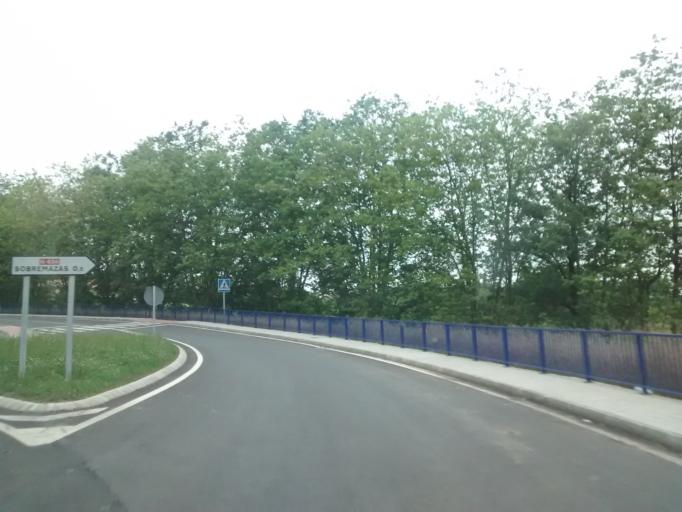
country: ES
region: Cantabria
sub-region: Provincia de Cantabria
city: Lierganes
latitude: 43.3667
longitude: -3.7569
